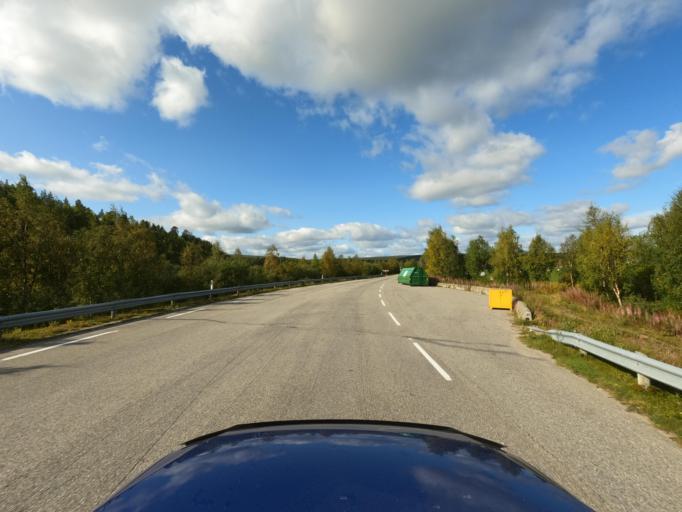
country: NO
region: Finnmark Fylke
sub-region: Karasjok
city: Karasjohka
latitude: 69.3983
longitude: 25.8406
